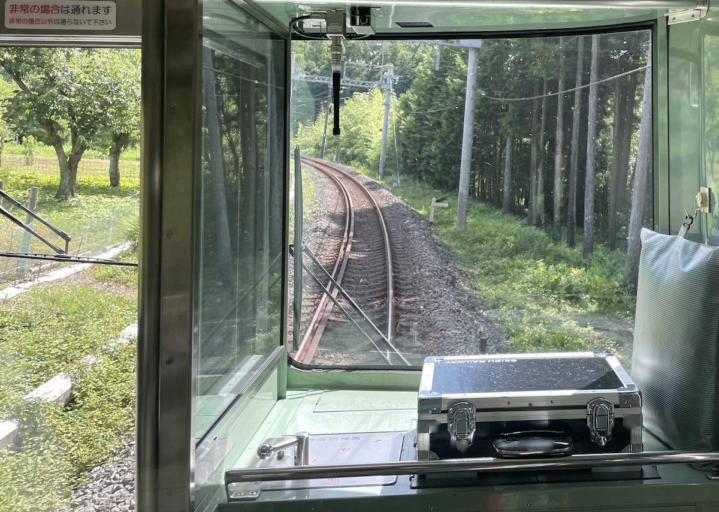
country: JP
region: Saitama
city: Hanno
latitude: 35.8861
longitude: 139.2725
